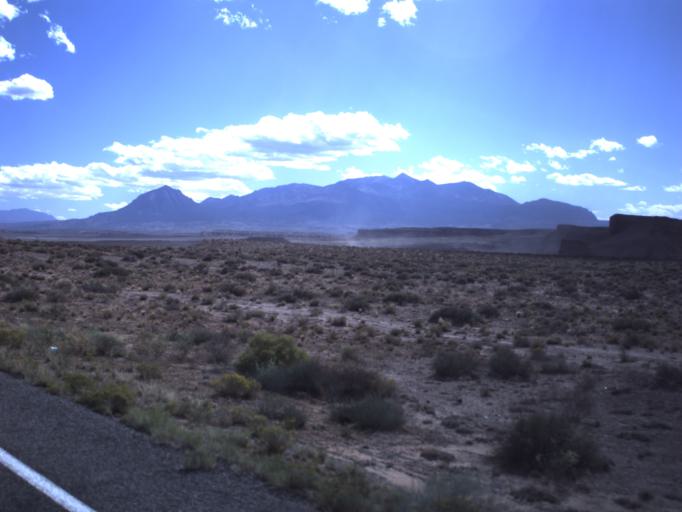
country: US
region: Utah
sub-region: Emery County
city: Ferron
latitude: 38.3431
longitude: -110.6918
